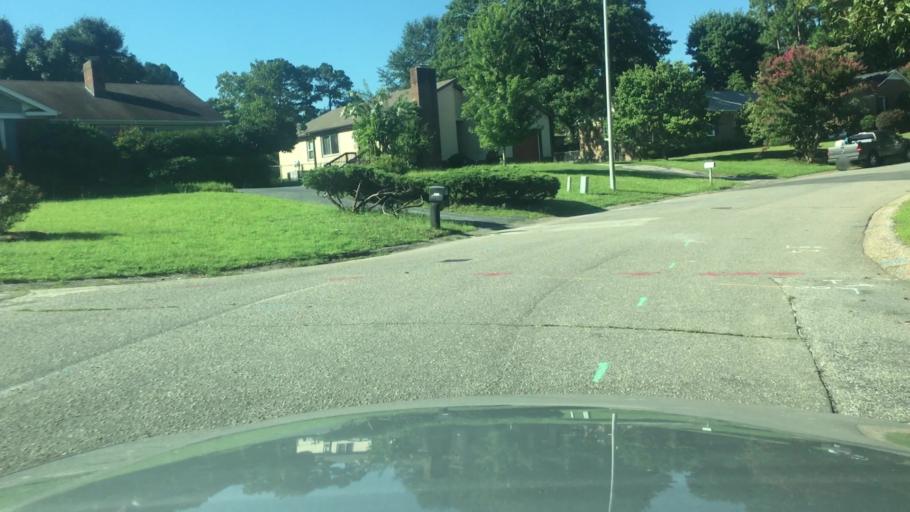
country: US
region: North Carolina
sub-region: Cumberland County
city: Spring Lake
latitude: 35.1373
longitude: -78.8934
